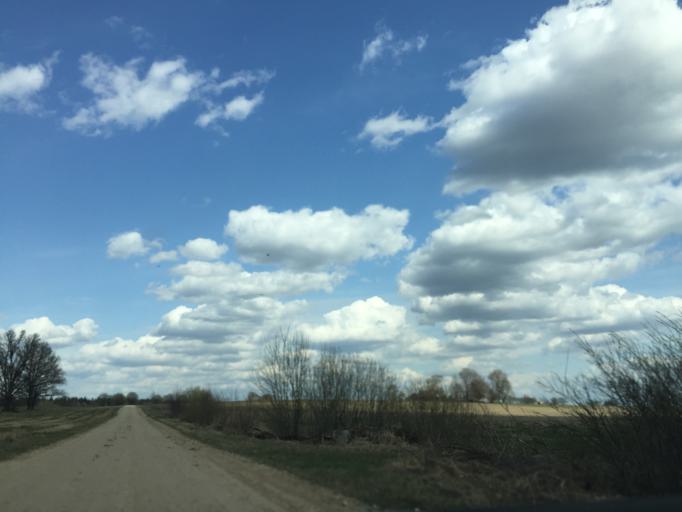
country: LV
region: Skriveri
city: Skriveri
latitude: 56.7571
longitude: 25.1271
